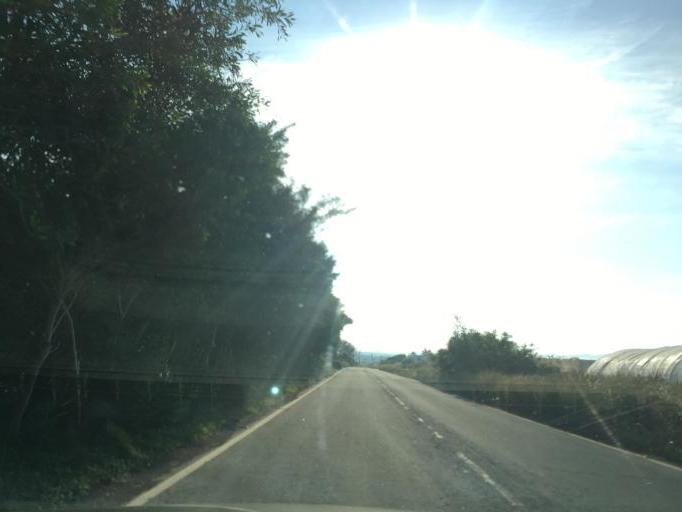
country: CY
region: Larnaka
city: Kofinou
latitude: 34.7329
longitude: 33.3575
